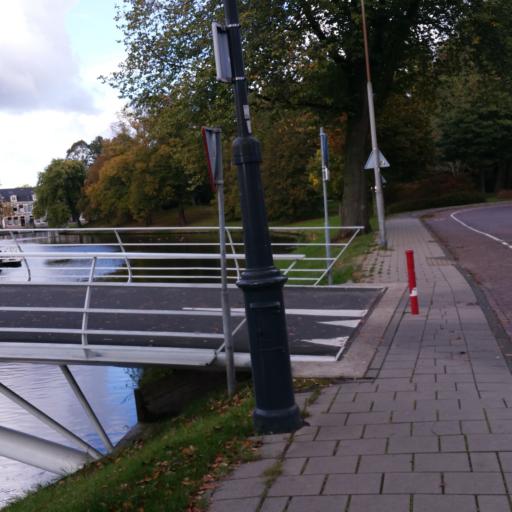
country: NL
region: North Holland
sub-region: Gemeente Haarlem
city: Haarlem
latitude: 52.3855
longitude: 4.6318
